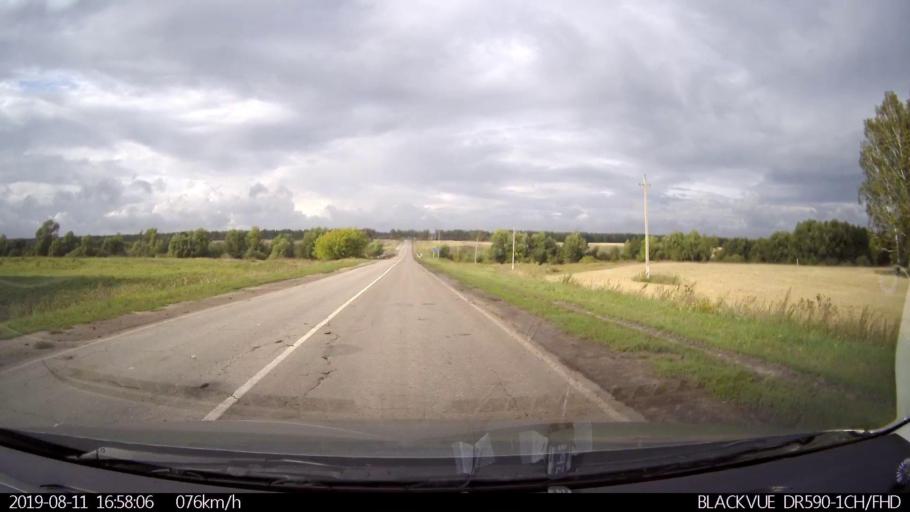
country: RU
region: Ulyanovsk
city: Mayna
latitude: 54.3050
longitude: 47.6552
